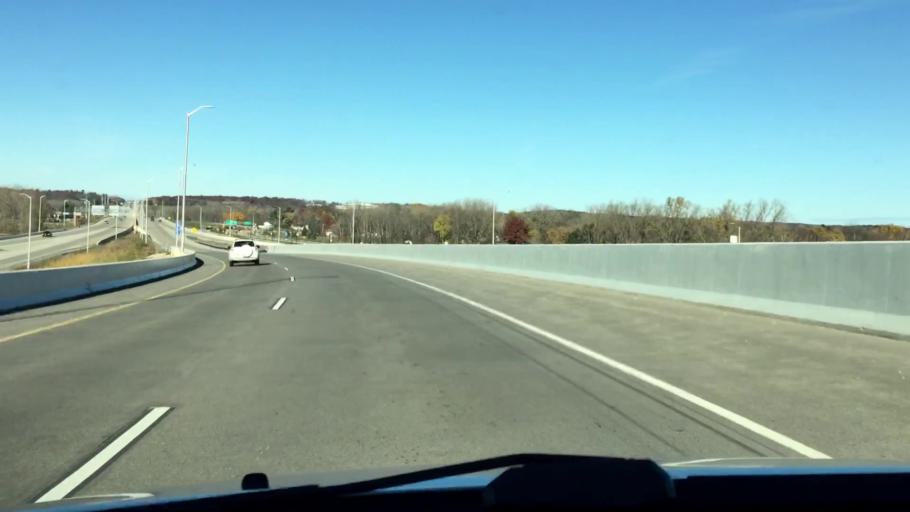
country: US
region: Wisconsin
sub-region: Brown County
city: Howard
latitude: 44.5398
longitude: -88.0801
